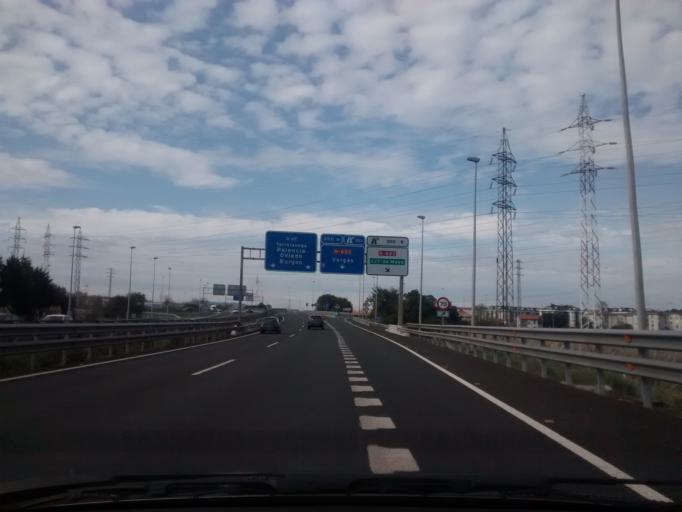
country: ES
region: Cantabria
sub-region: Provincia de Cantabria
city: Camargo
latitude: 43.4372
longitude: -3.8581
